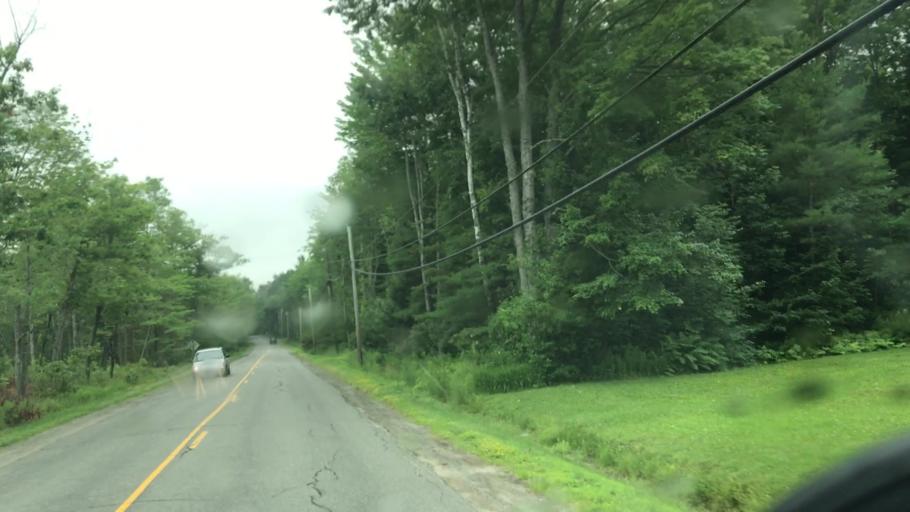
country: US
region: Maine
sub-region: Penobscot County
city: Orono
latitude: 44.8897
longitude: -68.7046
